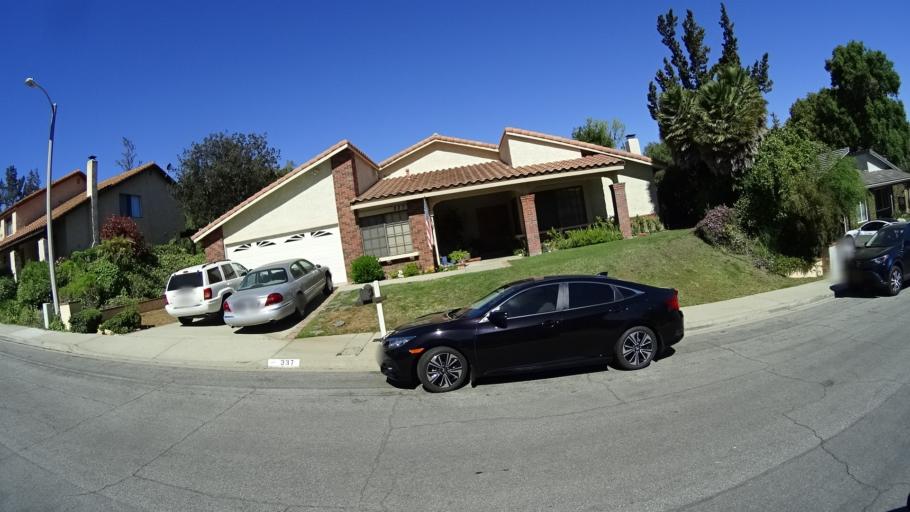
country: US
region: California
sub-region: Ventura County
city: Thousand Oaks
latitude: 34.1730
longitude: -118.8759
